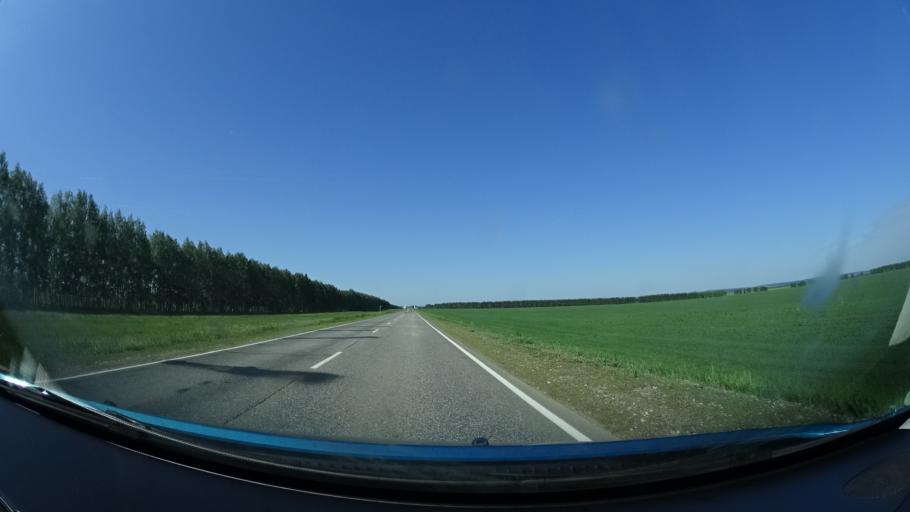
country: RU
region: Bashkortostan
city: Starobaltachevo
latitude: 55.9069
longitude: 55.7632
